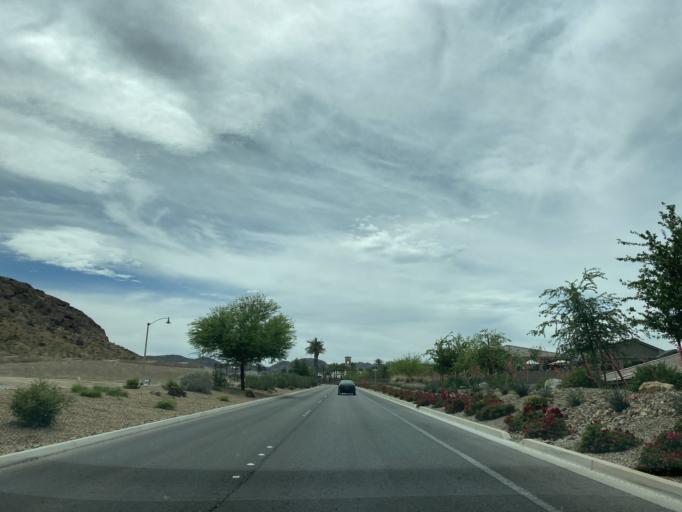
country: US
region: Nevada
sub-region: Clark County
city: Henderson
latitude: 36.0907
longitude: -114.9331
